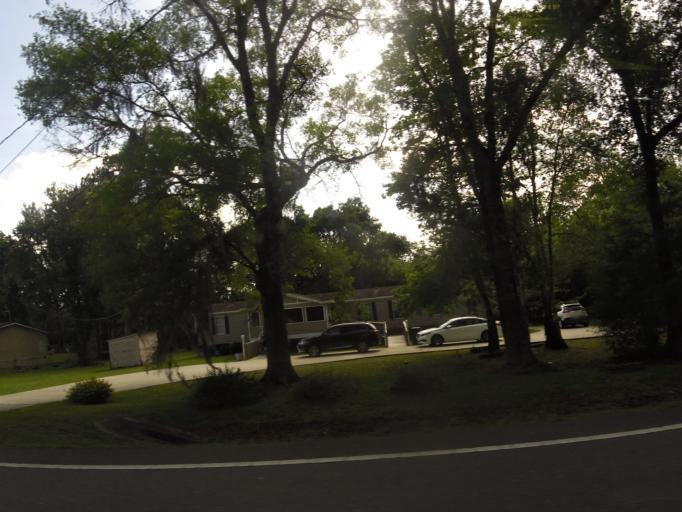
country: US
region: Florida
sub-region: Nassau County
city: Callahan
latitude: 30.5737
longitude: -81.8451
